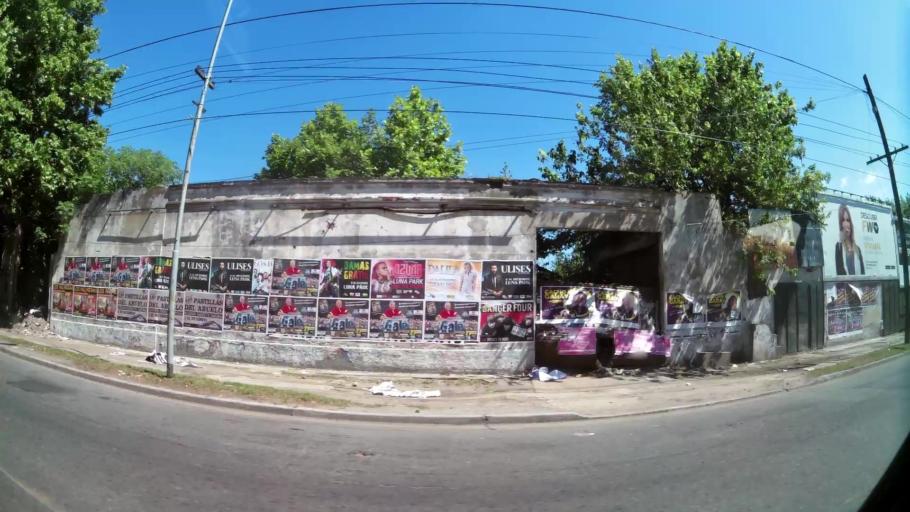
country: AR
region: Buenos Aires
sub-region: Partido de Tigre
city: Tigre
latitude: -34.4313
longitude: -58.5624
